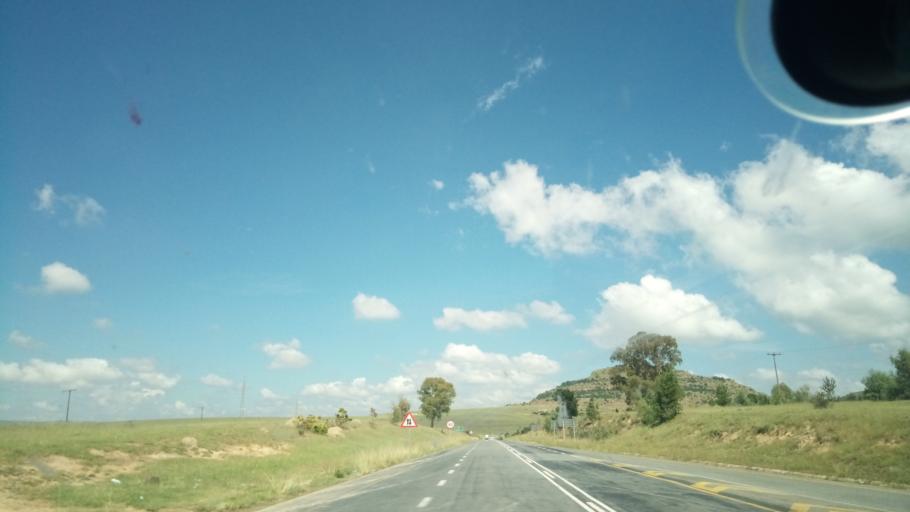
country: ZA
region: Orange Free State
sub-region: Thabo Mofutsanyana District Municipality
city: Ficksburg
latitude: -28.8910
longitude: 27.8555
